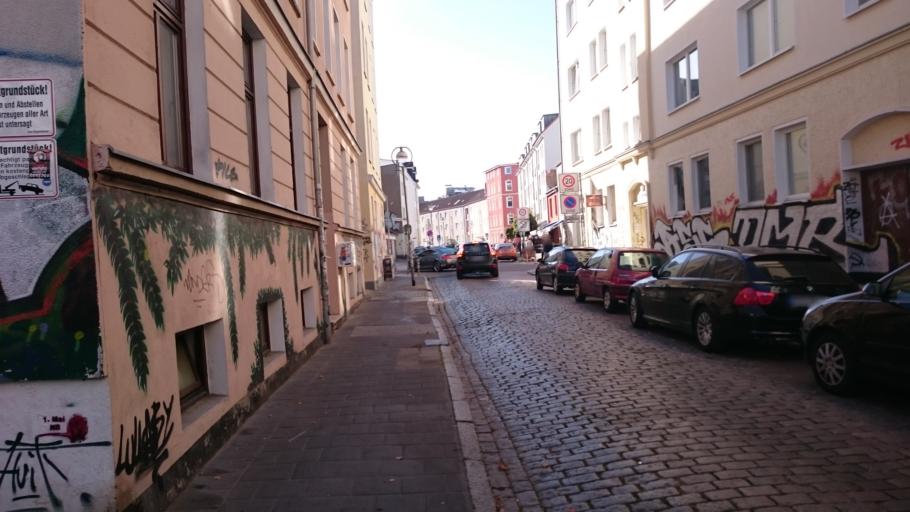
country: DE
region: Mecklenburg-Vorpommern
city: Rostock
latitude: 54.0882
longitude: 12.1177
